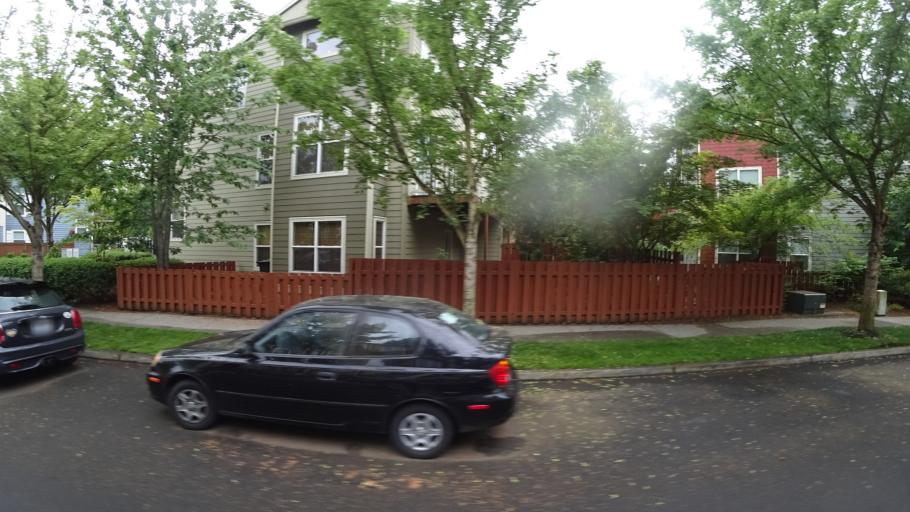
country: US
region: Oregon
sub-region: Washington County
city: Rockcreek
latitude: 45.5351
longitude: -122.8904
